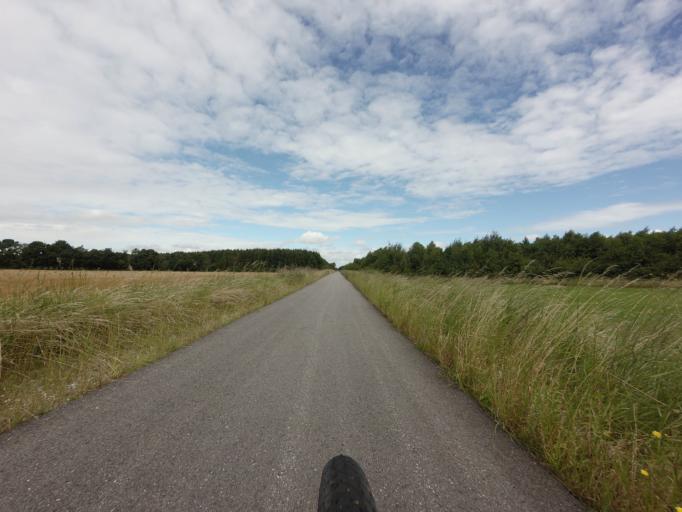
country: DK
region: Central Jutland
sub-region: Norddjurs Kommune
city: Auning
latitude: 56.4129
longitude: 10.3922
